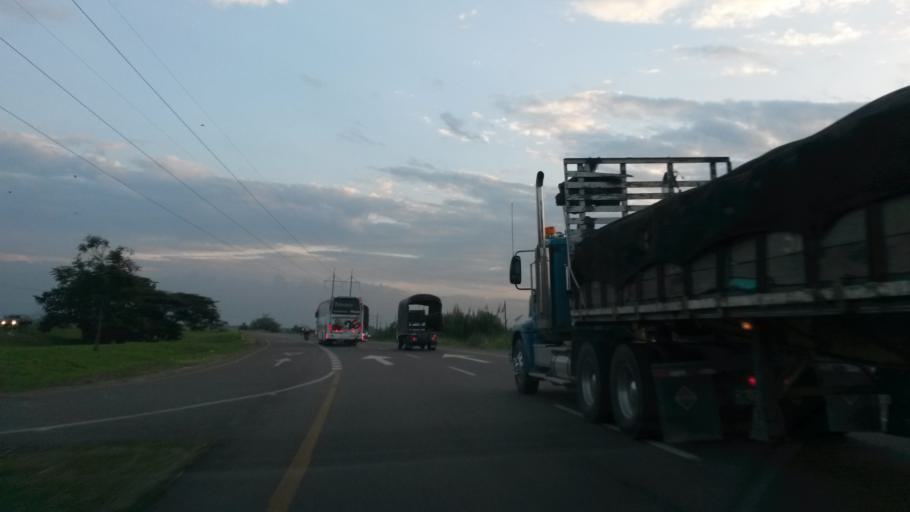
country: CO
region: Cauca
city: Caloto
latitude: 3.0955
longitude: -76.4696
